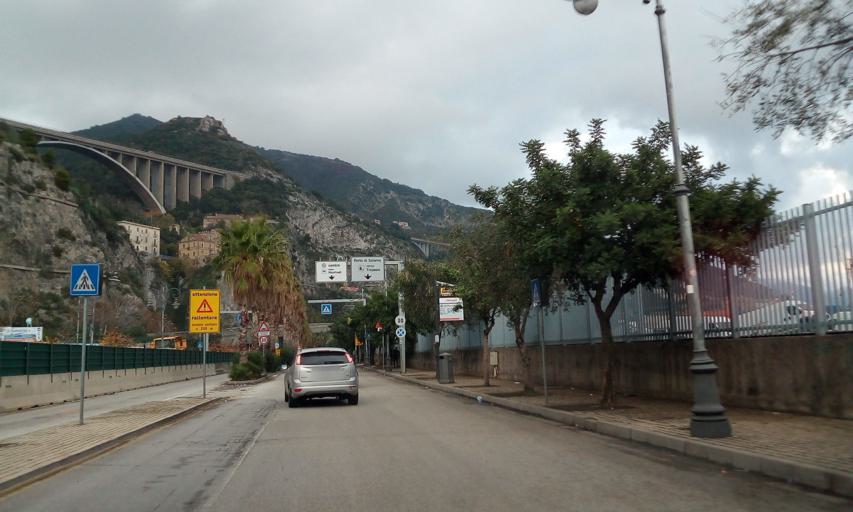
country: IT
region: Campania
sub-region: Provincia di Salerno
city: Vietri sul Mare
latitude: 40.6725
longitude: 14.7366
